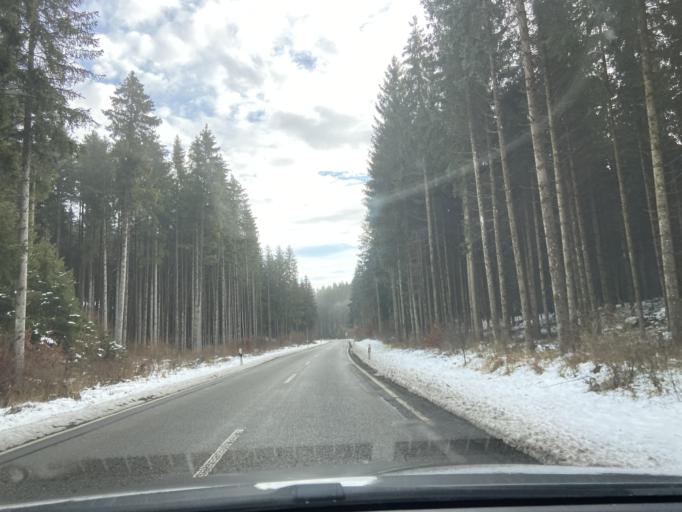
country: DE
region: Baden-Wuerttemberg
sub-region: Tuebingen Region
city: Pfronstetten
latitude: 48.2437
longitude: 9.3434
